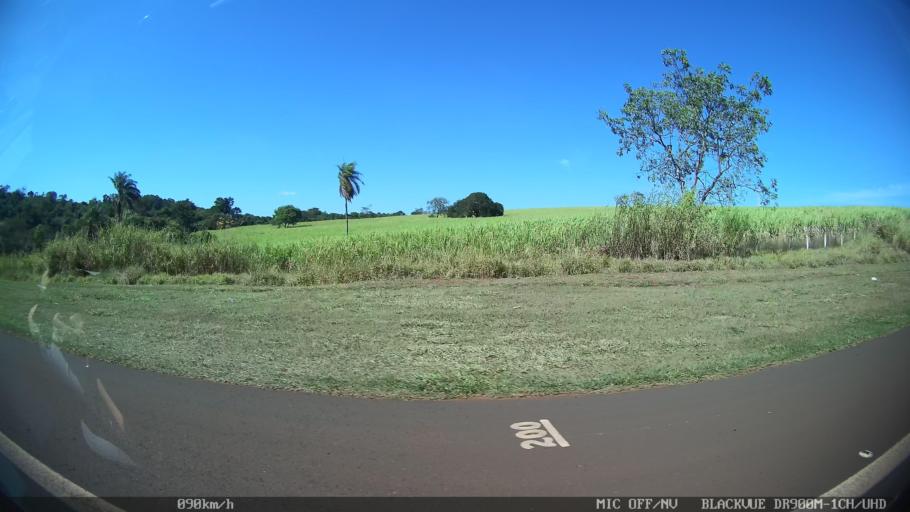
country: BR
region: Sao Paulo
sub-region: Franca
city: Franca
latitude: -20.6360
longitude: -47.4708
